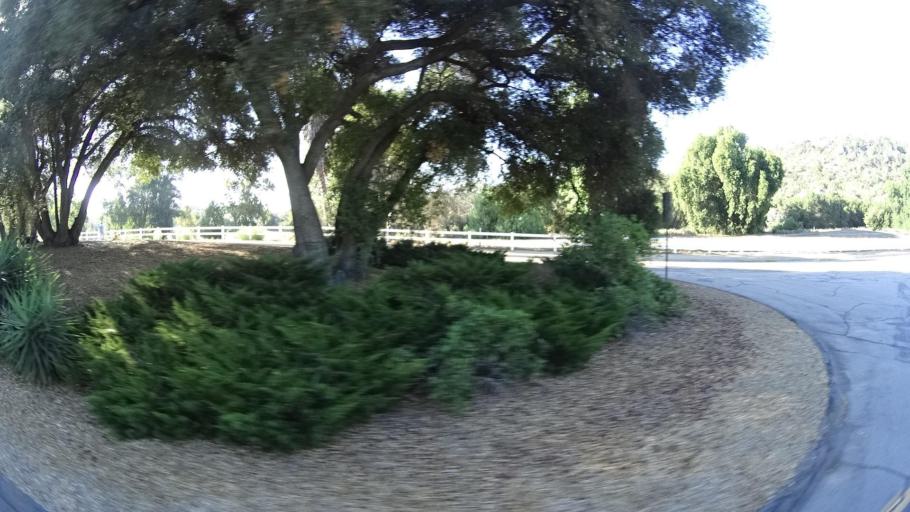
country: US
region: California
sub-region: San Diego County
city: Hidden Meadows
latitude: 33.2155
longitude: -117.1119
